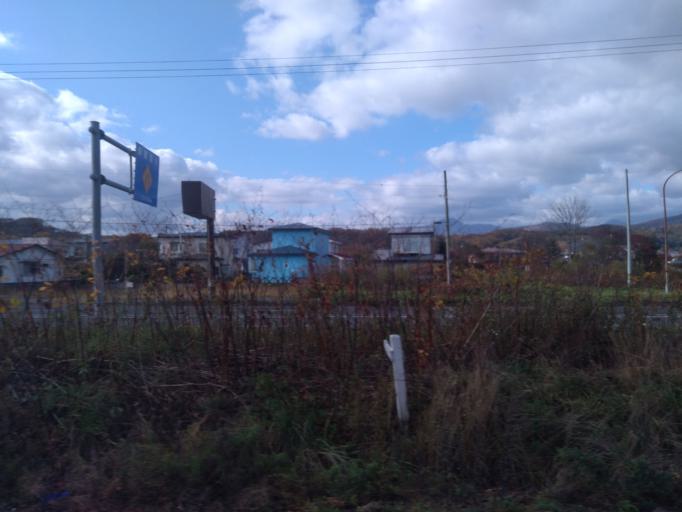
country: JP
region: Hokkaido
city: Shiraoi
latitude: 42.4476
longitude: 141.1738
